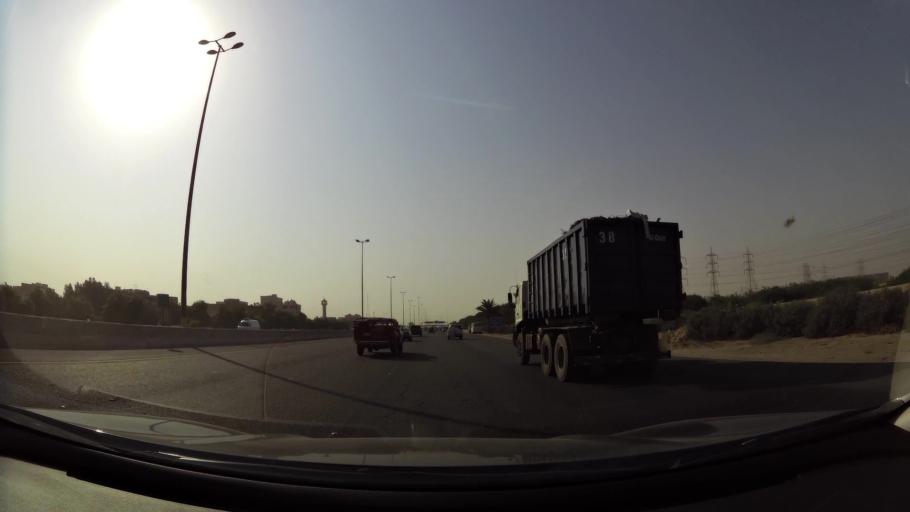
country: KW
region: Al Ahmadi
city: Al Ahmadi
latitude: 29.1015
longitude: 48.0965
